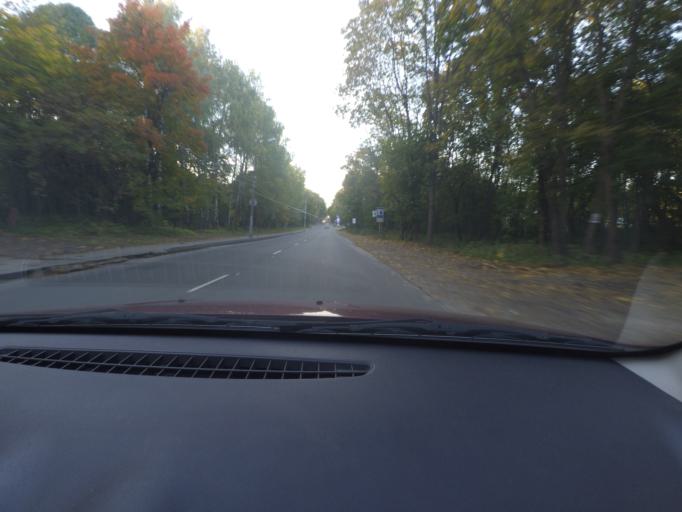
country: RU
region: Nizjnij Novgorod
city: Nizhniy Novgorod
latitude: 56.2661
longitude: 43.9975
